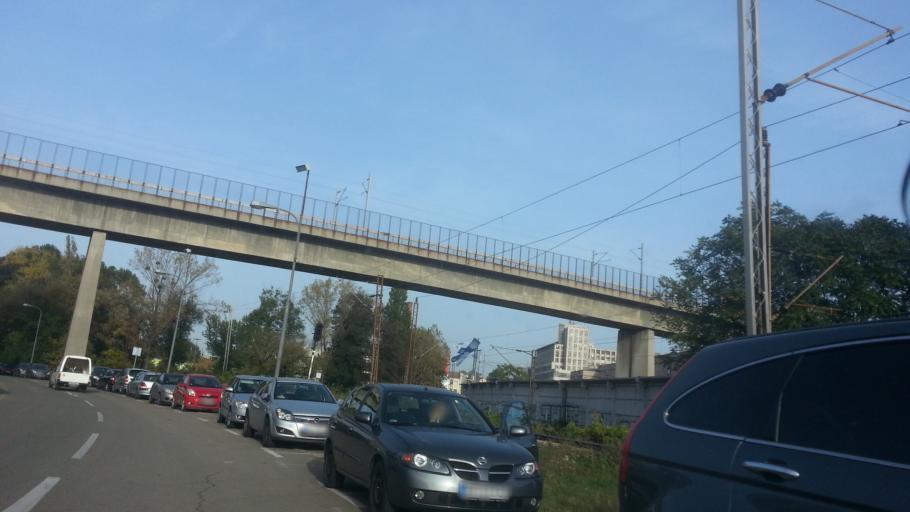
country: RS
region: Central Serbia
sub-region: Belgrade
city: Novi Beograd
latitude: 44.7963
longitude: 20.4397
